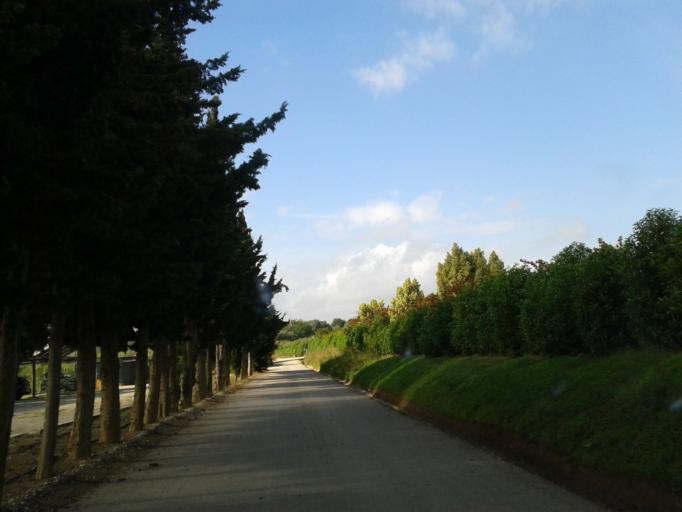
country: PT
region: Faro
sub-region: Tavira
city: Tavira
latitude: 37.1576
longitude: -7.5691
